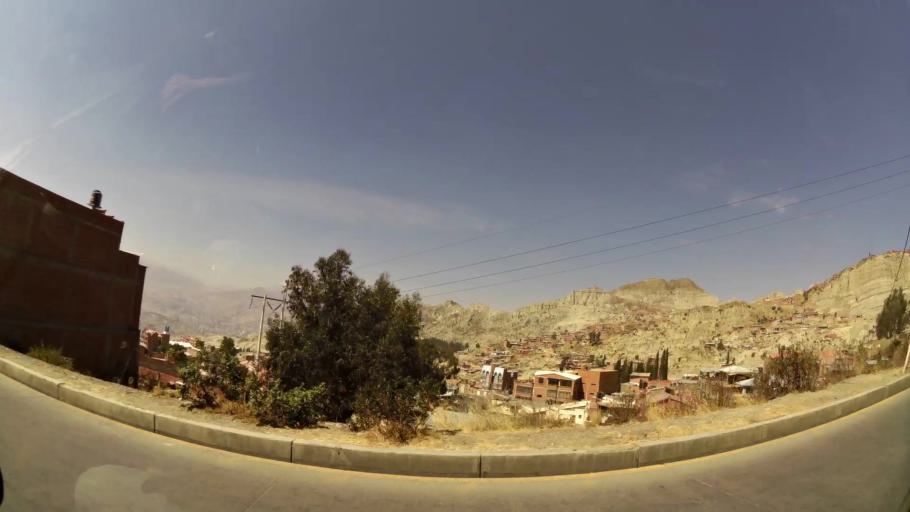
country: BO
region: La Paz
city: La Paz
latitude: -16.5330
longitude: -68.1357
